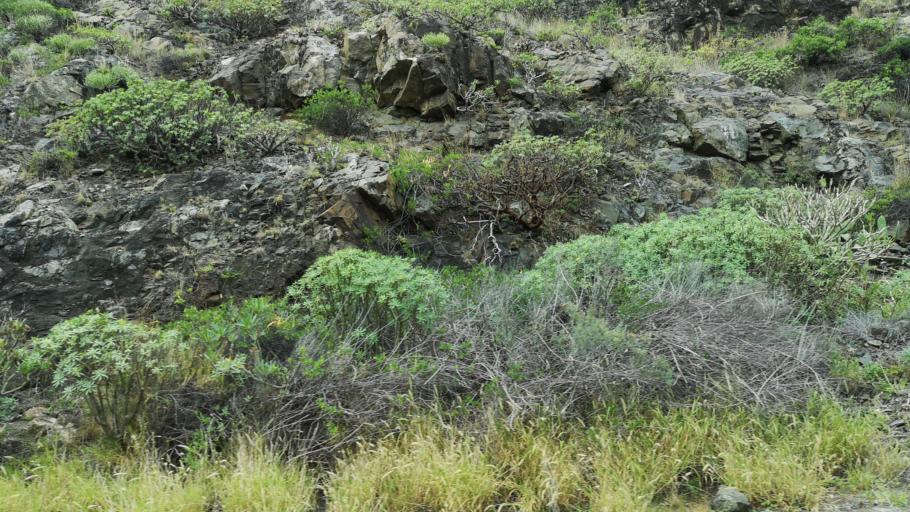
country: ES
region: Canary Islands
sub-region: Provincia de Santa Cruz de Tenerife
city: Vallehermosa
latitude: 28.1961
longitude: -17.2579
